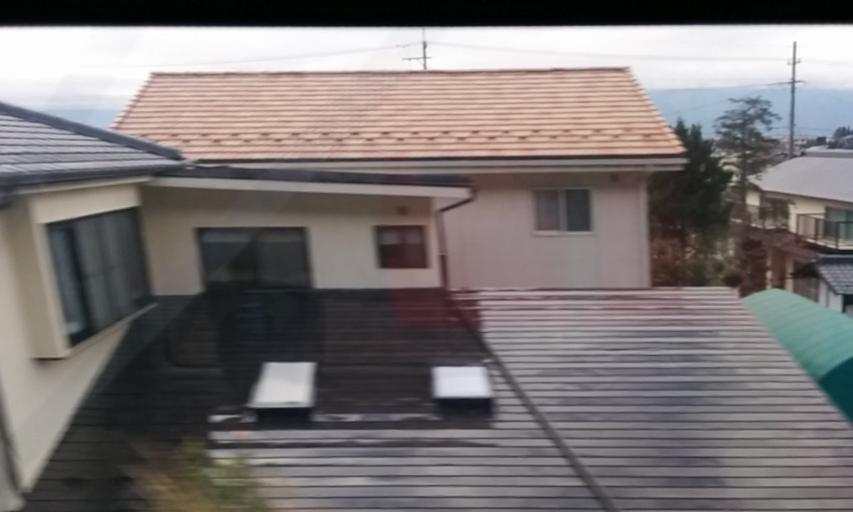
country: JP
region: Nagano
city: Matsumoto
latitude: 36.2544
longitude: 137.9513
